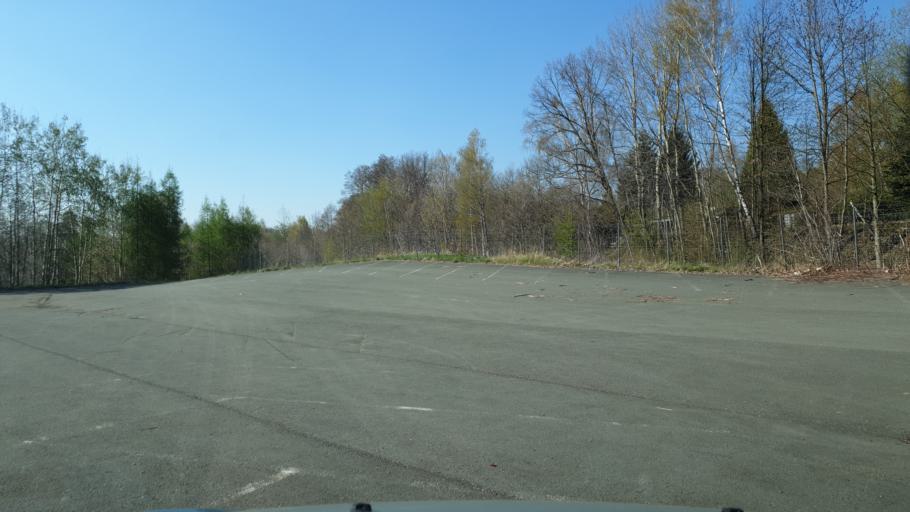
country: DE
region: Saxony
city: Hohndorf
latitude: 50.7380
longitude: 12.6882
